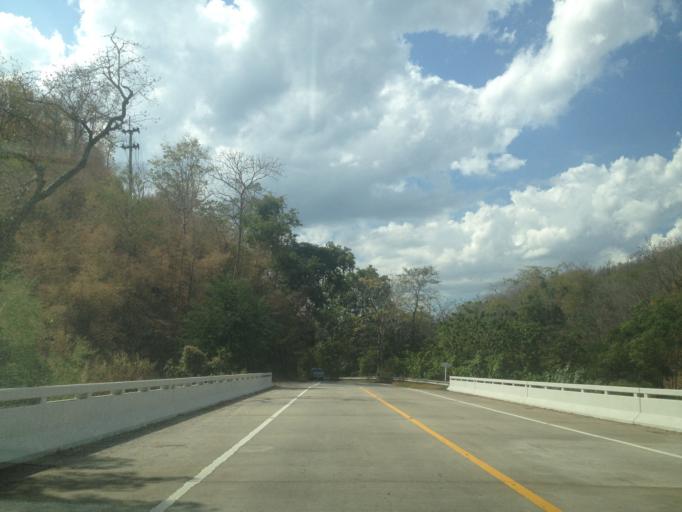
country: TH
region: Chiang Mai
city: Hot
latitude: 18.2323
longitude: 98.5246
